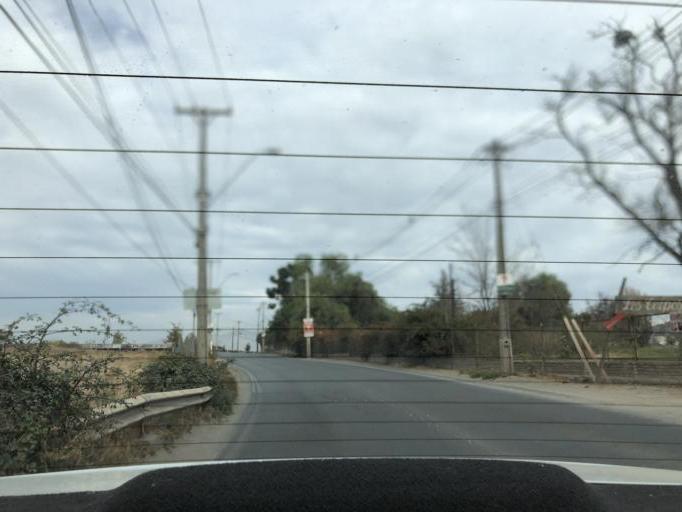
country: CL
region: Santiago Metropolitan
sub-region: Provincia de Cordillera
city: Puente Alto
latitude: -33.6053
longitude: -70.5339
